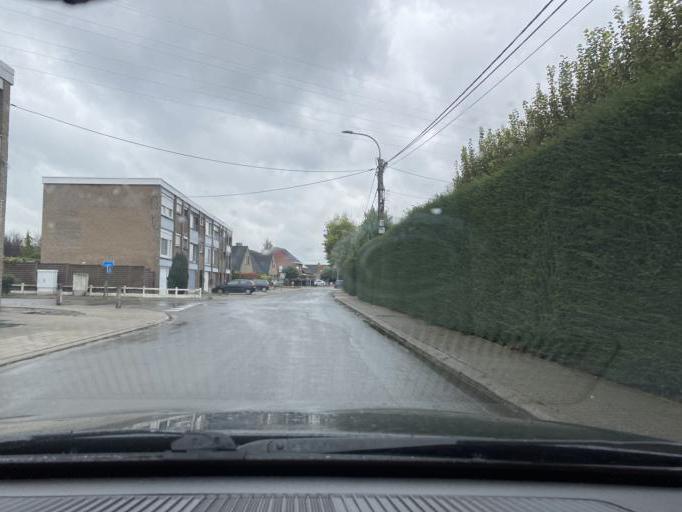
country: BE
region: Flanders
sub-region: Provincie West-Vlaanderen
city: Wielsbeke
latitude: 50.9157
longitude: 3.3997
